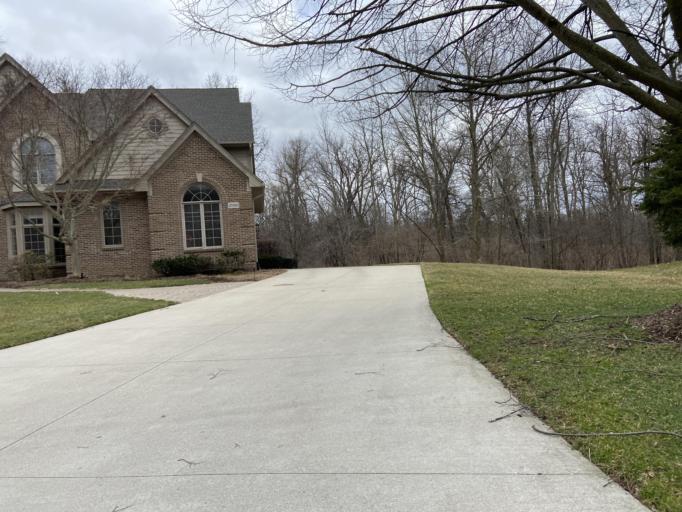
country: US
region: Michigan
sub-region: Oakland County
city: Franklin
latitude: 42.5019
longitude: -83.3231
